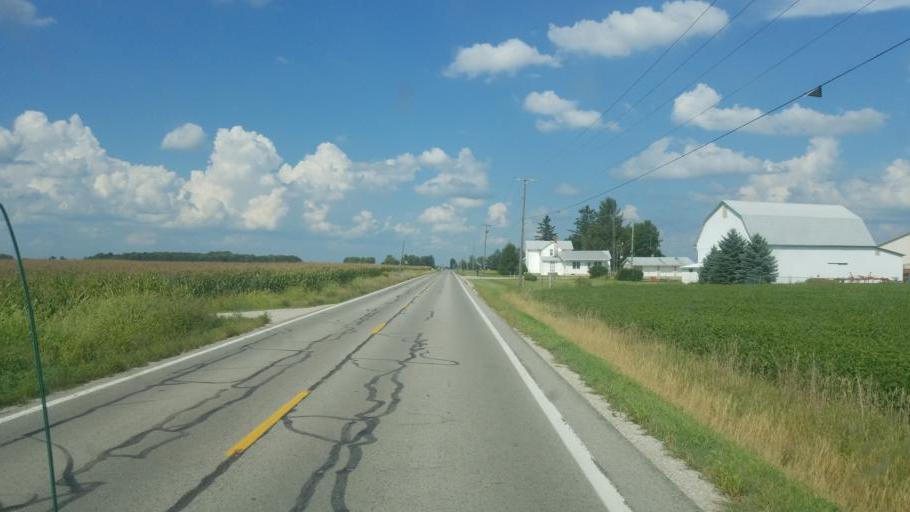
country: US
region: Ohio
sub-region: Huron County
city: Willard
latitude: 41.0023
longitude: -82.9185
